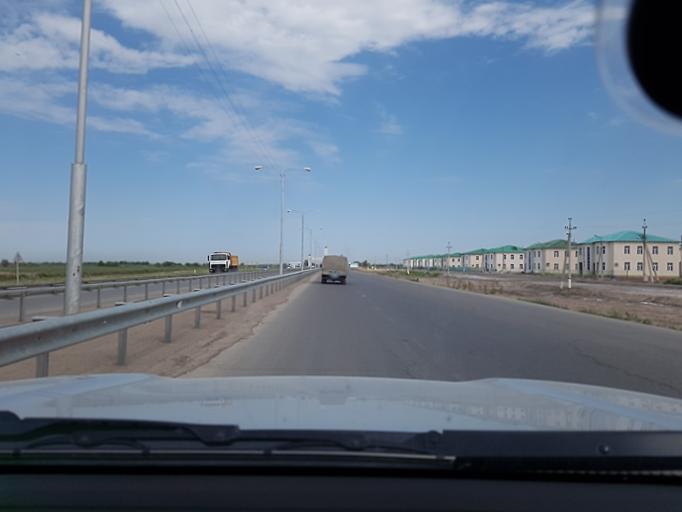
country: TM
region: Dasoguz
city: Dasoguz
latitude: 41.8851
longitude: 59.9418
